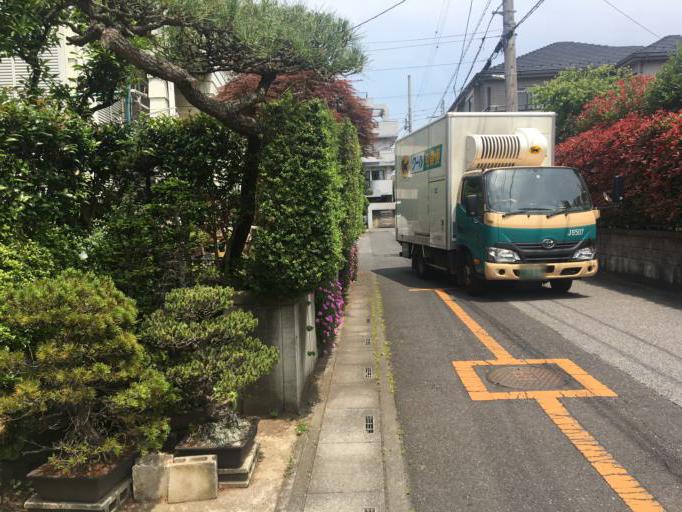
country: JP
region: Saitama
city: Koshigaya
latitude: 35.9027
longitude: 139.7776
